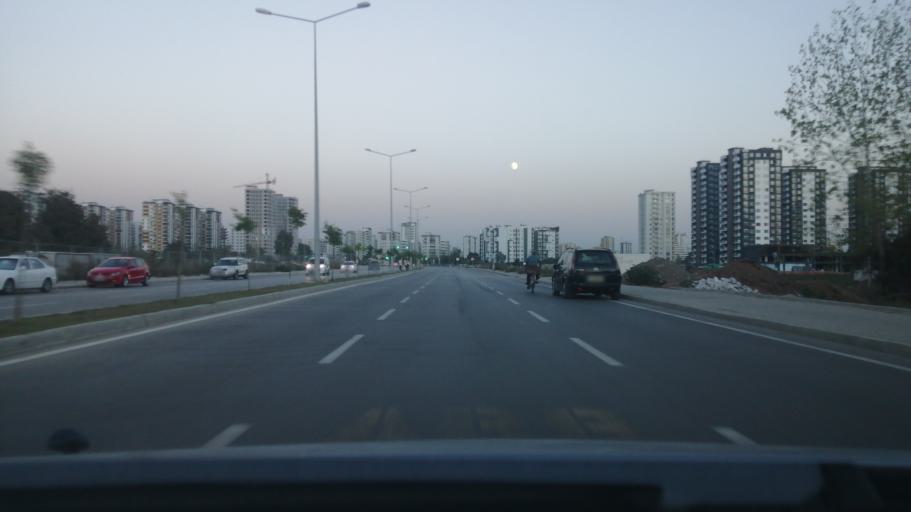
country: TR
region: Adana
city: Seyhan
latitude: 37.0152
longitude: 35.2542
